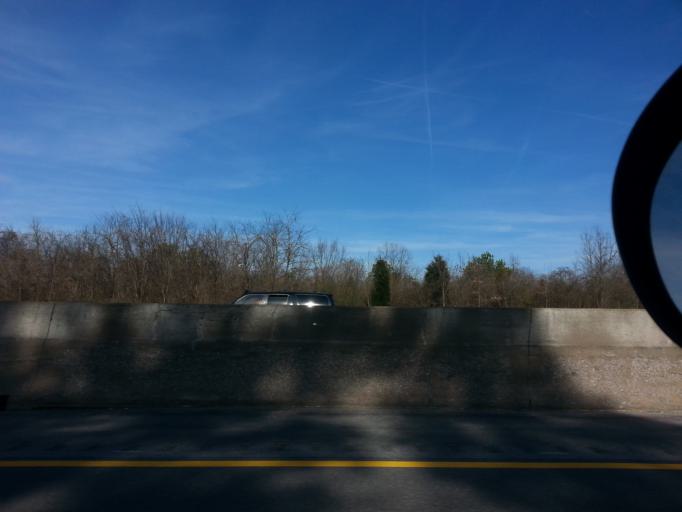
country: US
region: Tennessee
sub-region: Williamson County
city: Brentwood Estates
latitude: 36.0605
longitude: -86.6804
